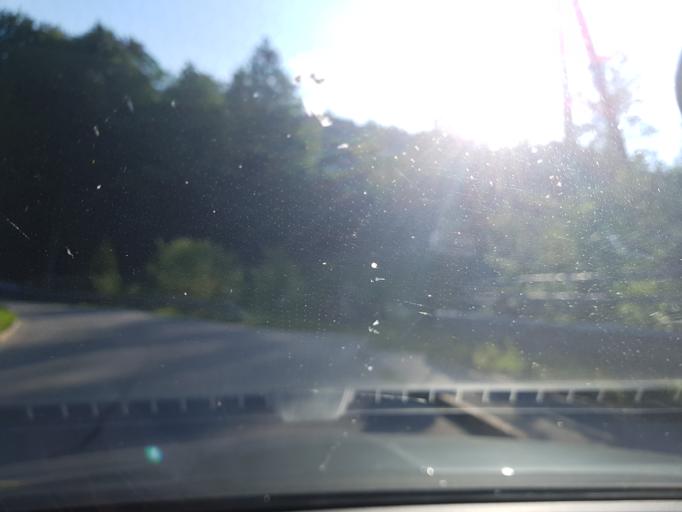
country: DE
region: Bavaria
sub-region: Upper Bavaria
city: Berchtesgaden
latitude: 47.6471
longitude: 13.0029
